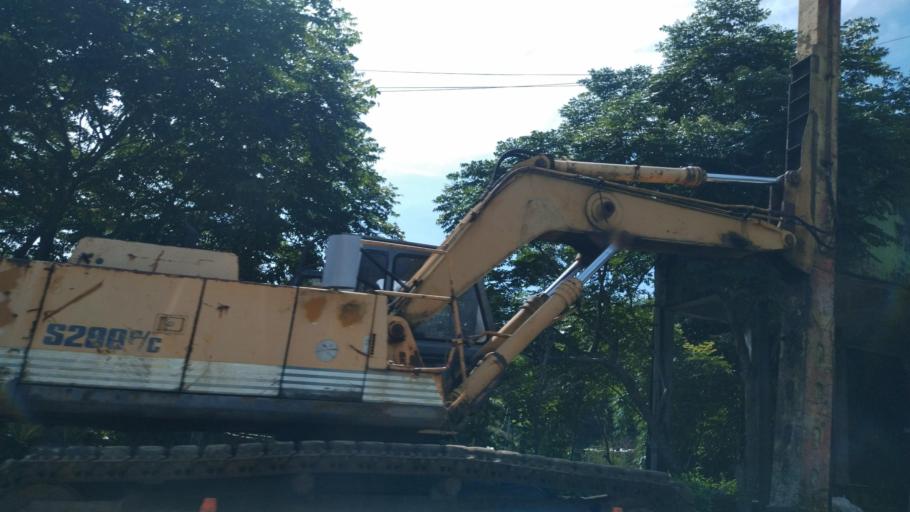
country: TW
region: Taipei
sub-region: Taipei
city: Banqiao
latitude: 24.9505
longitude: 121.5053
